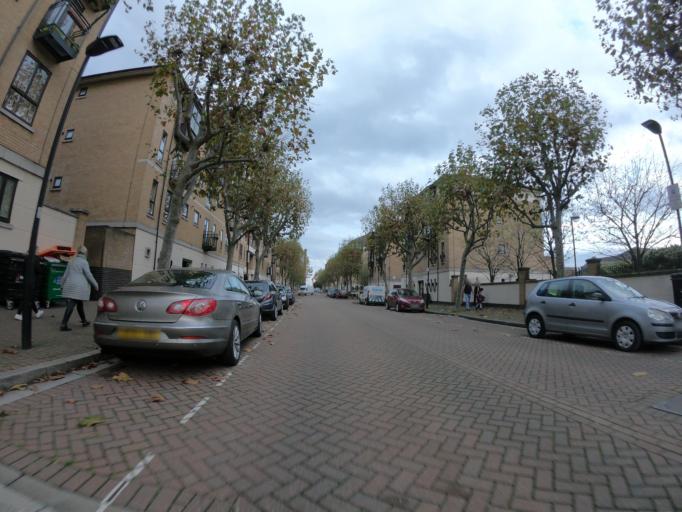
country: GB
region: England
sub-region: Greater London
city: East Ham
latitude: 51.5048
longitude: 0.0238
